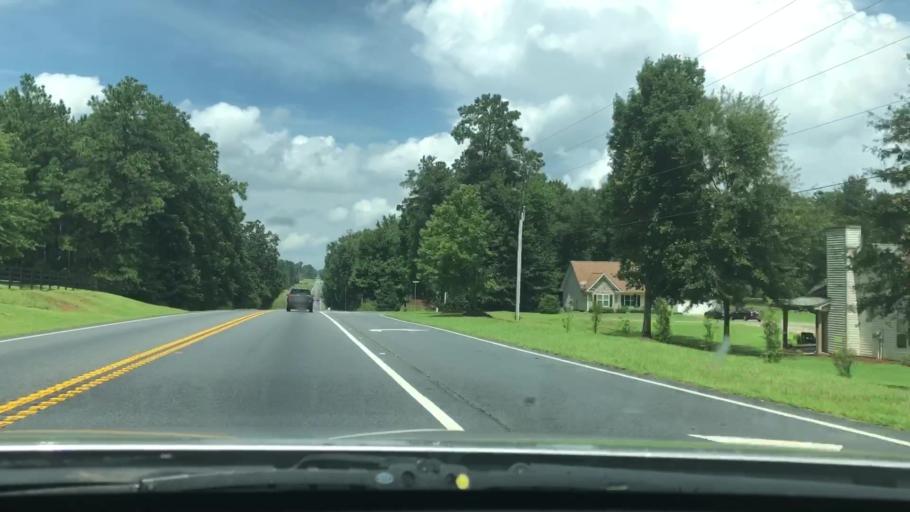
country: US
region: Georgia
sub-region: Lamar County
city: Barnesville
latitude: 33.1020
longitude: -84.1548
